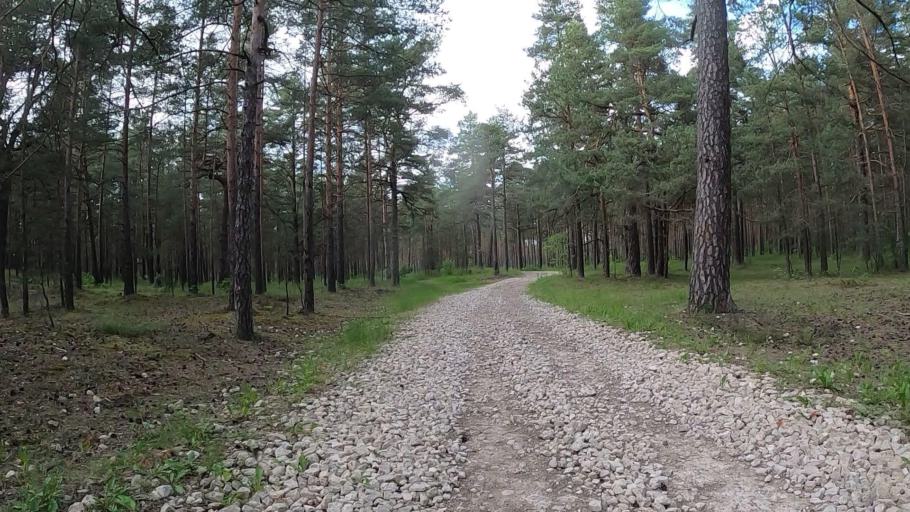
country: LV
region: Riga
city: Jaunciems
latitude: 57.0467
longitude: 24.1152
